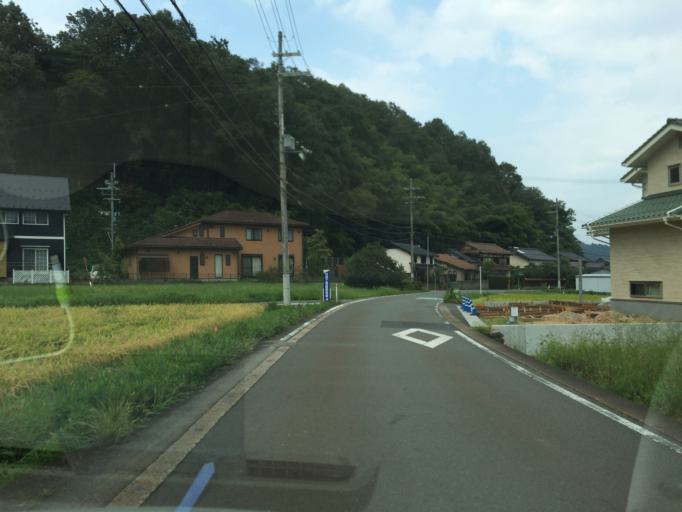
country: JP
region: Hyogo
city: Toyooka
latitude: 35.4803
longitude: 134.7768
